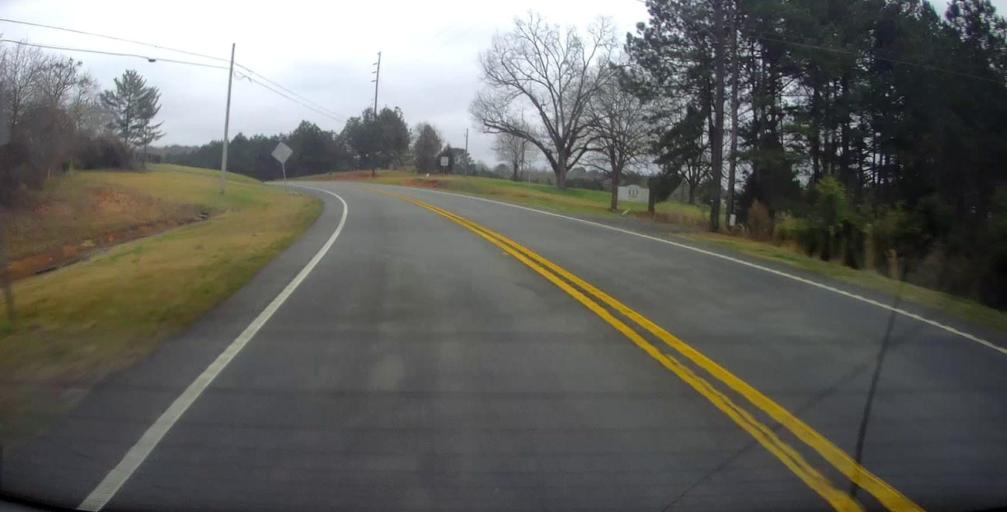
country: US
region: Georgia
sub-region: Pike County
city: Zebulon
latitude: 33.1021
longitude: -84.3603
